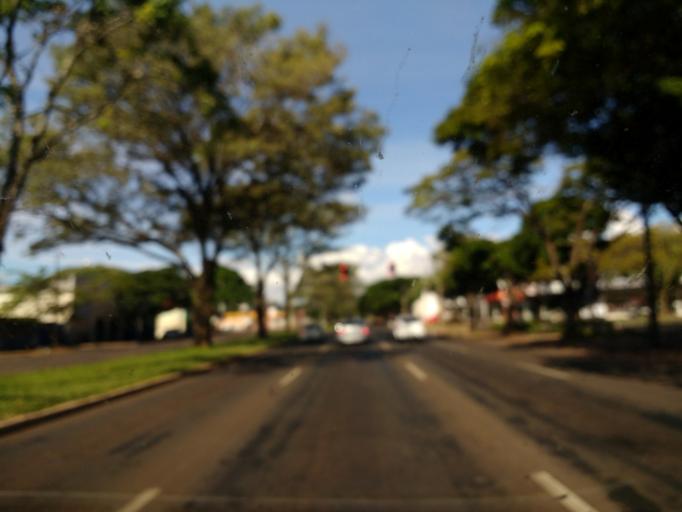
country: BR
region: Parana
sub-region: Maringa
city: Maringa
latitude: -23.4172
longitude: -51.9192
